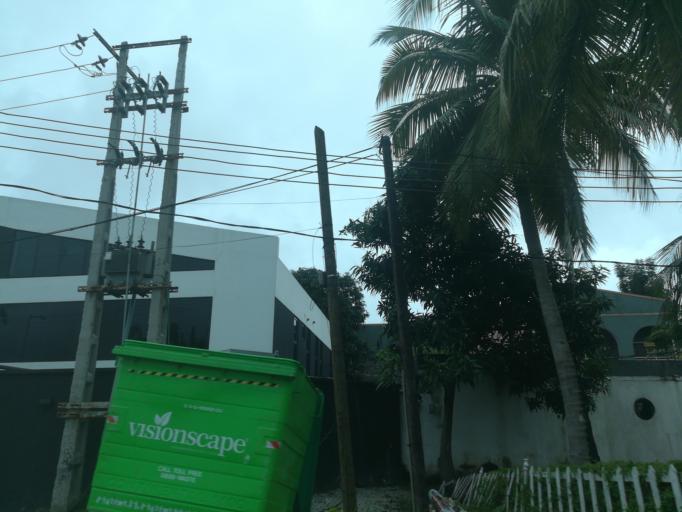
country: NG
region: Lagos
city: Ikoyi
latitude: 6.4260
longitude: 3.4209
